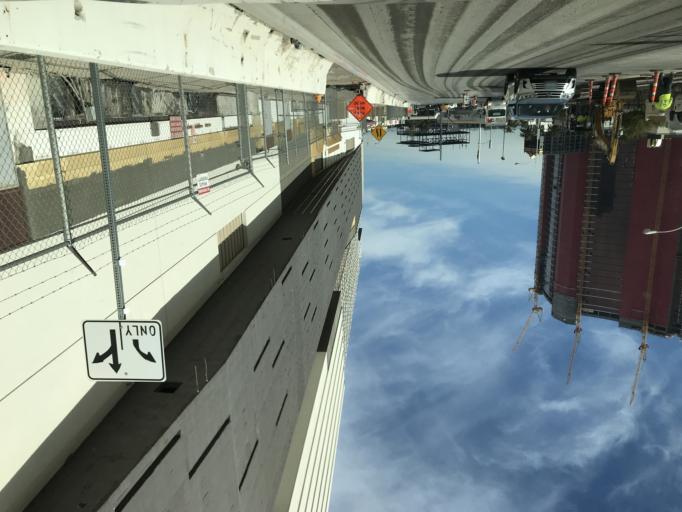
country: US
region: Nevada
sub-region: Clark County
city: Paradise
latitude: 36.1363
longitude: -115.1602
